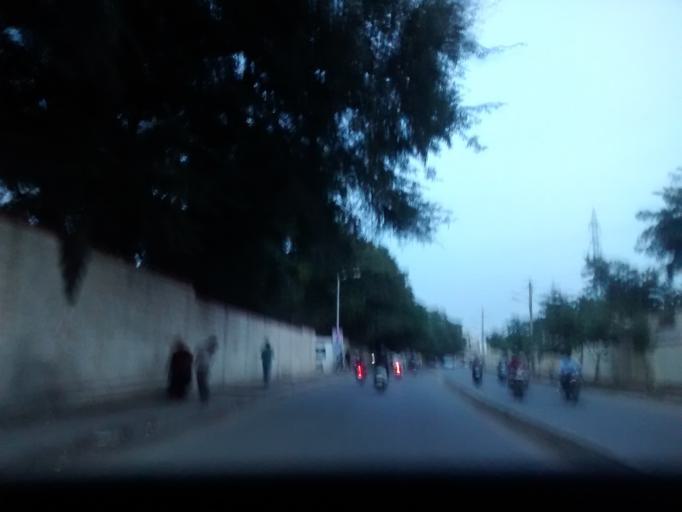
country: IN
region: Karnataka
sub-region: Bangalore Urban
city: Bangalore
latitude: 12.9755
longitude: 77.6675
